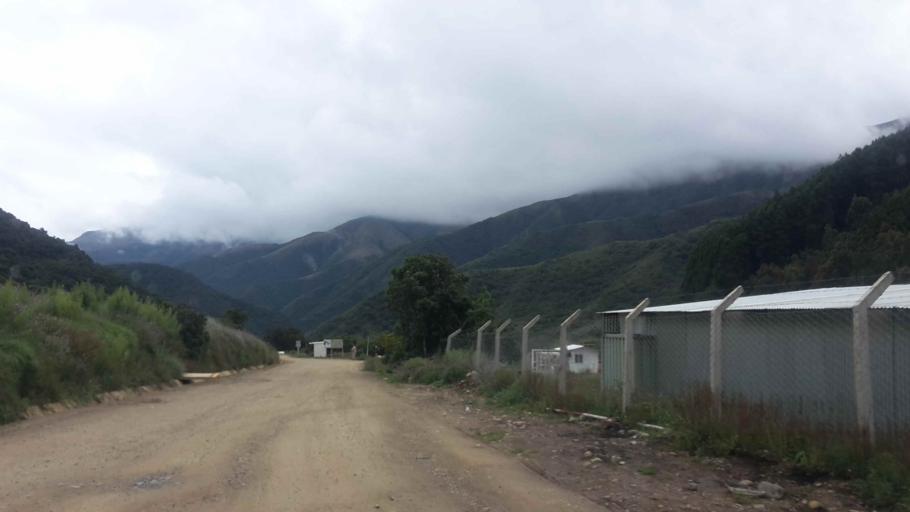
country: BO
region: Cochabamba
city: Totora
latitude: -17.5722
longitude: -65.2827
